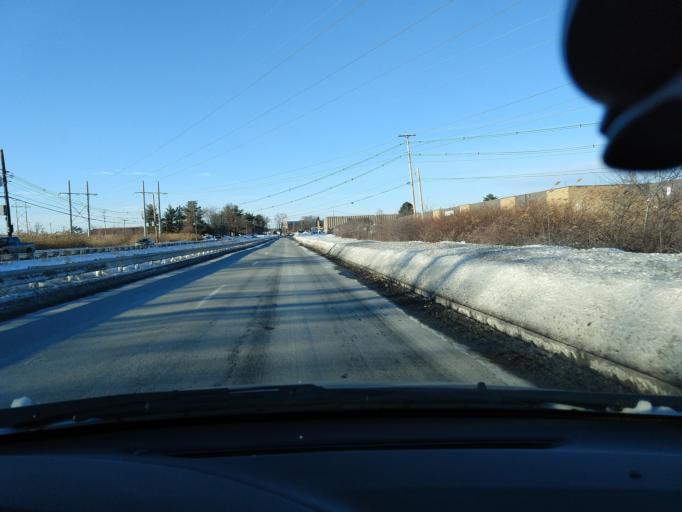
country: US
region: Massachusetts
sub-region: Middlesex County
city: Woburn
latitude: 42.5108
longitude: -71.1331
